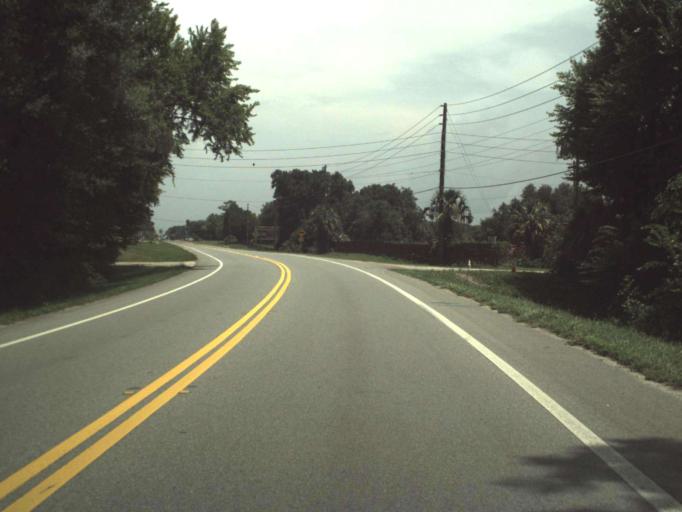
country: US
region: Florida
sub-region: Sumter County
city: Wildwood
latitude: 28.8029
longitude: -82.0457
